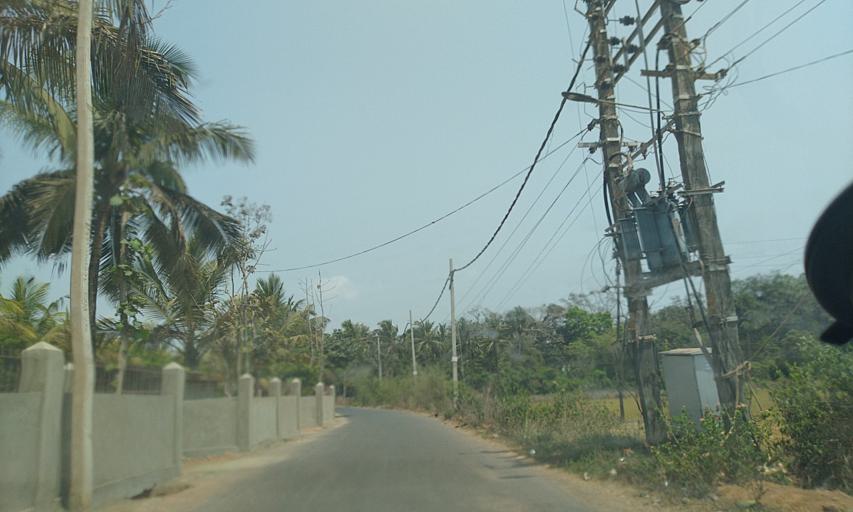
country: IN
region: Goa
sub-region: North Goa
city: Saligao
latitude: 15.5530
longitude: 73.8110
